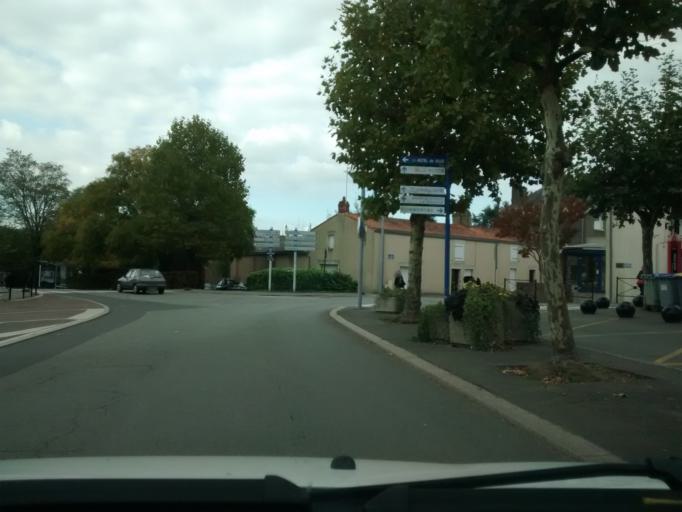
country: FR
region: Pays de la Loire
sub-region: Departement de la Loire-Atlantique
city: Coueron
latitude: 47.2119
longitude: -1.7266
